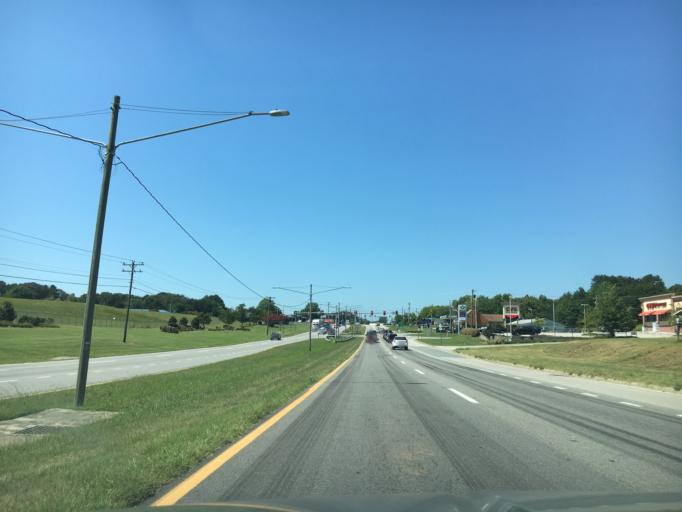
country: US
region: Virginia
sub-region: City of Danville
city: Danville
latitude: 36.5810
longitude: -79.3384
